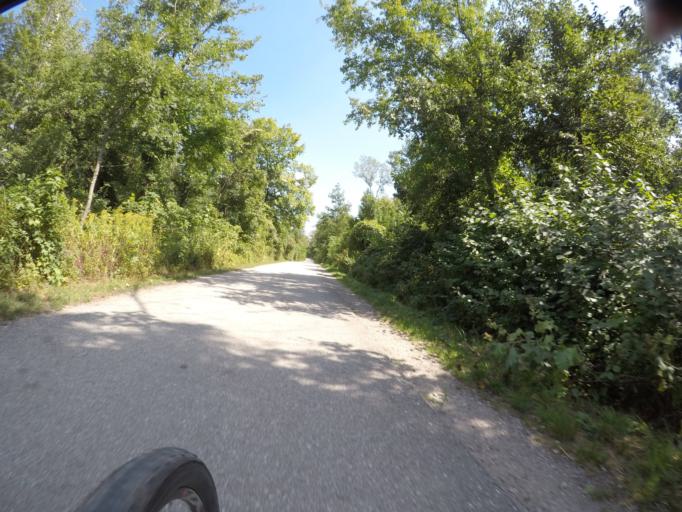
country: AT
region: Lower Austria
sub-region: Politischer Bezirk Ganserndorf
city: Gross-Enzersdorf
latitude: 48.1898
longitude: 16.5346
